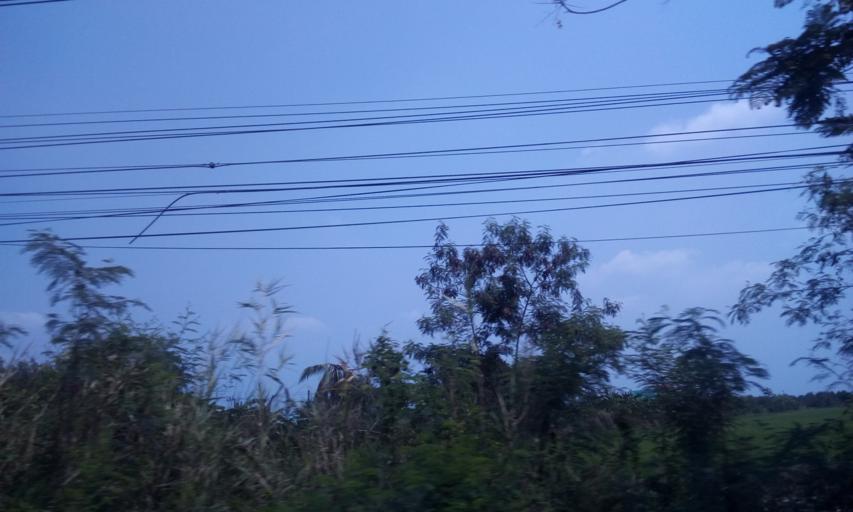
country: TH
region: Chachoengsao
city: Chachoengsao
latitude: 13.7572
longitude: 101.0746
